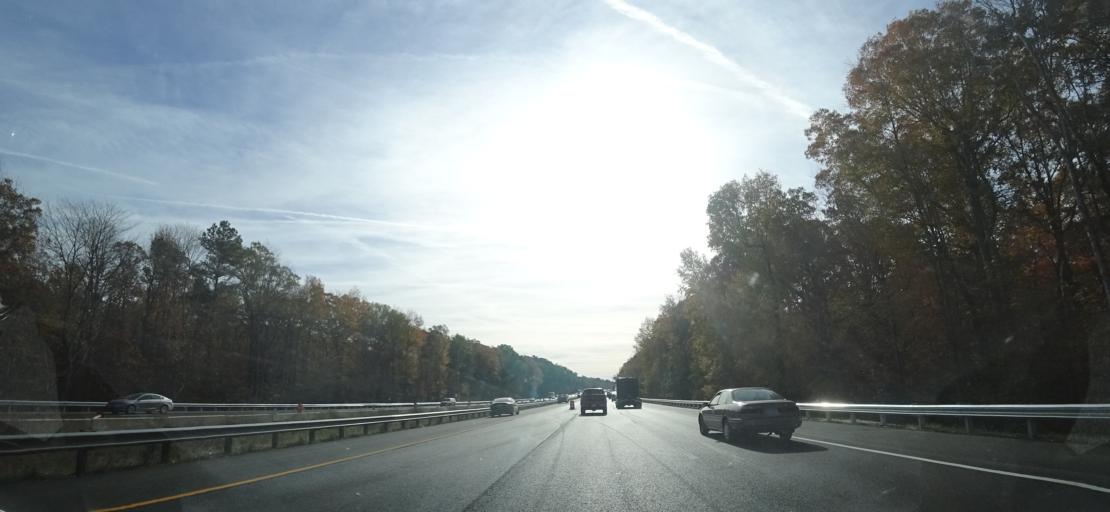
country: US
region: Virginia
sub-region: York County
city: Yorktown
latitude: 37.1592
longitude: -76.5408
